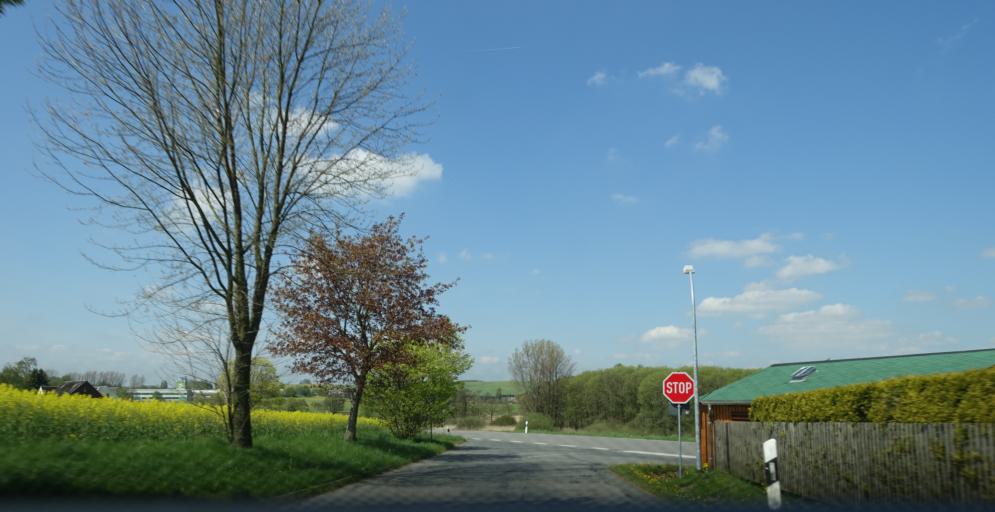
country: DE
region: Saxony
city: Grosshartmannsdorf
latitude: 50.8022
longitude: 13.3375
